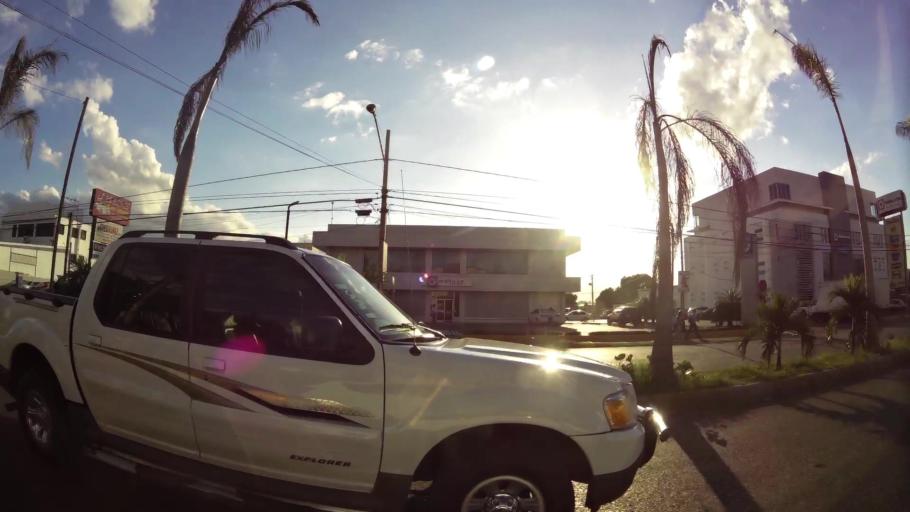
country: DO
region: Santiago
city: Santiago de los Caballeros
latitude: 19.4772
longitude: -70.7167
